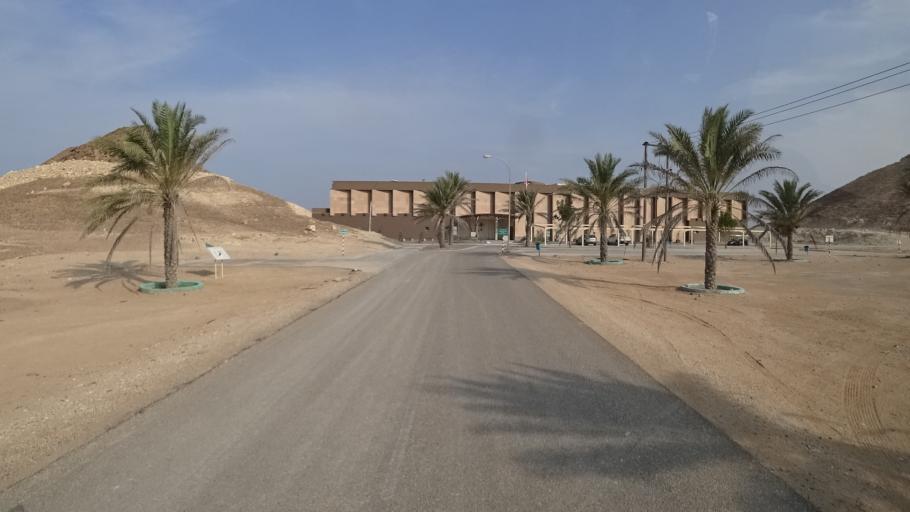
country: OM
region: Ash Sharqiyah
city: Sur
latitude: 22.4266
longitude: 59.8267
